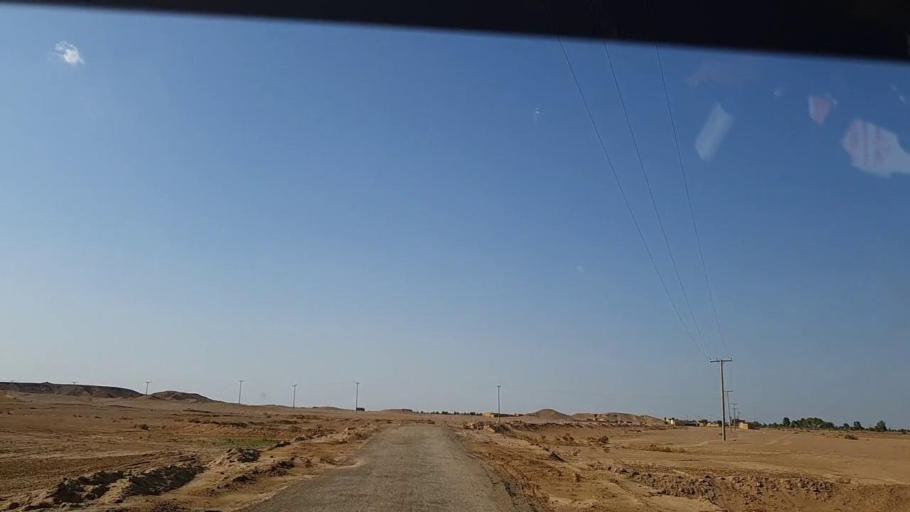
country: PK
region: Sindh
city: Johi
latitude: 26.5385
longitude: 67.5084
